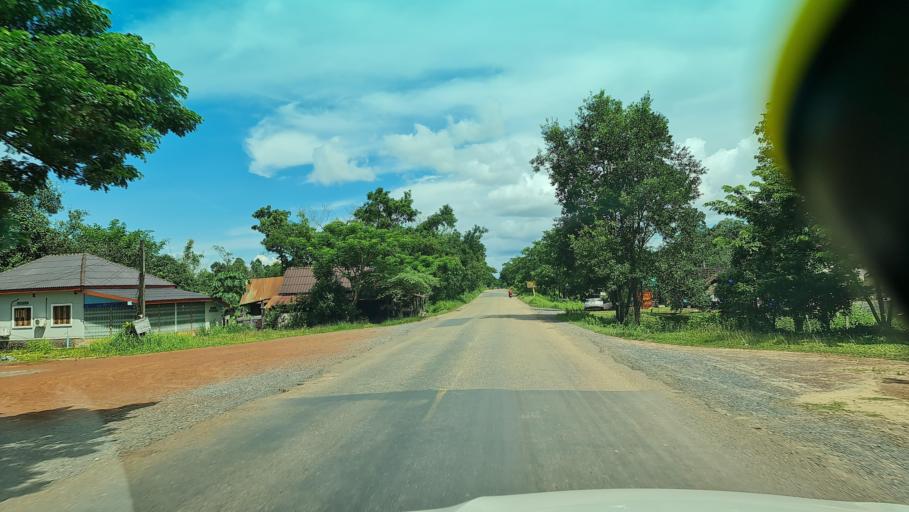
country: LA
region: Bolikhamxai
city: Ban Nahin
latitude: 18.2293
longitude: 104.1932
